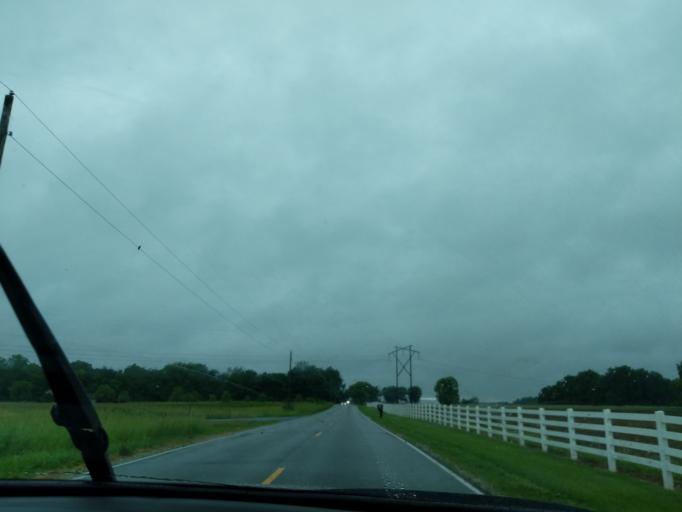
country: US
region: Indiana
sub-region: Hamilton County
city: Noblesville
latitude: 40.0661
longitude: -85.9487
